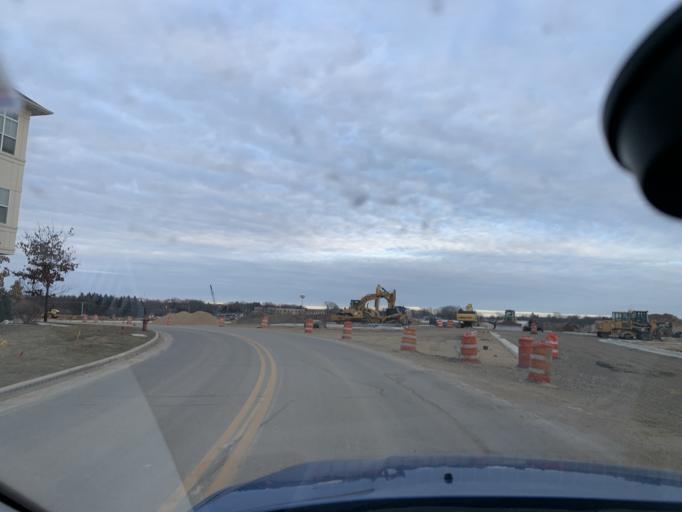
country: US
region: Wisconsin
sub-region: Dane County
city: Verona
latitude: 42.9860
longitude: -89.5539
